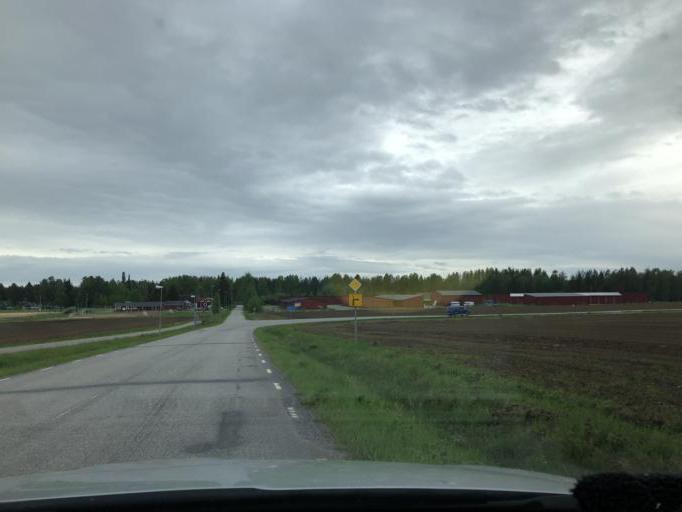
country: SE
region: Norrbotten
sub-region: Pitea Kommun
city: Bergsviken
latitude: 65.3814
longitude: 21.3131
